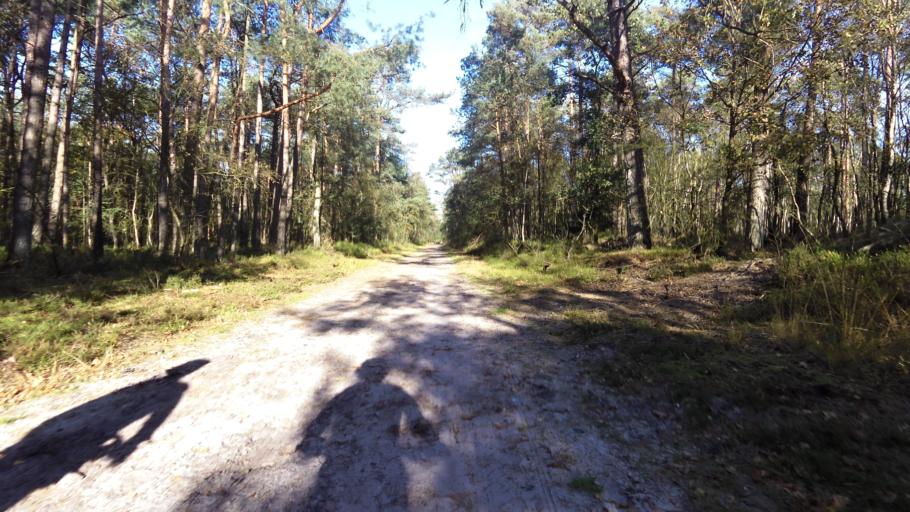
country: NL
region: Gelderland
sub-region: Gemeente Epe
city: Epe
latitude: 52.3723
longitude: 5.9457
